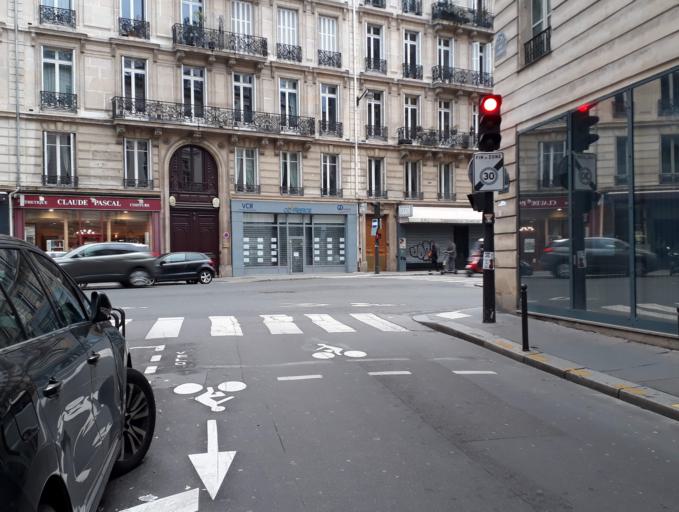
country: FR
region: Ile-de-France
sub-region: Paris
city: Paris
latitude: 48.8744
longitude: 2.3371
